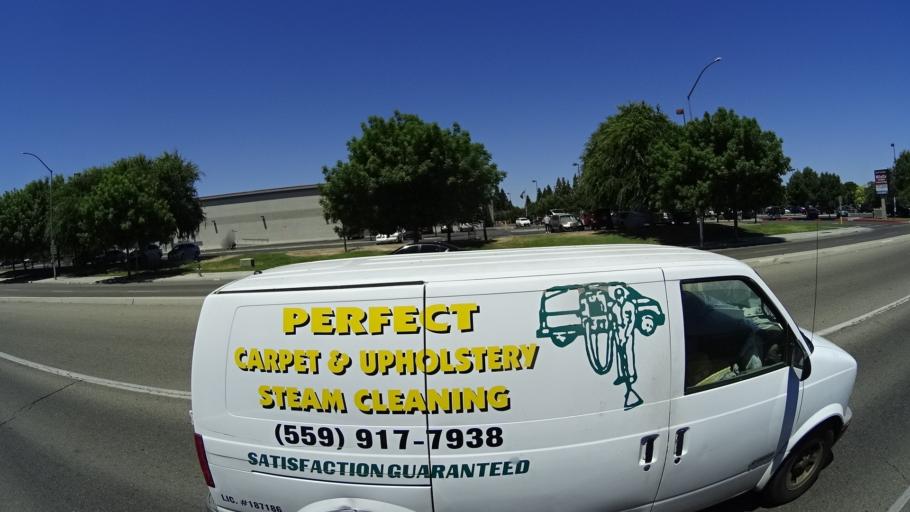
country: US
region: California
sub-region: Fresno County
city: Sunnyside
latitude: 36.7333
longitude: -119.7183
